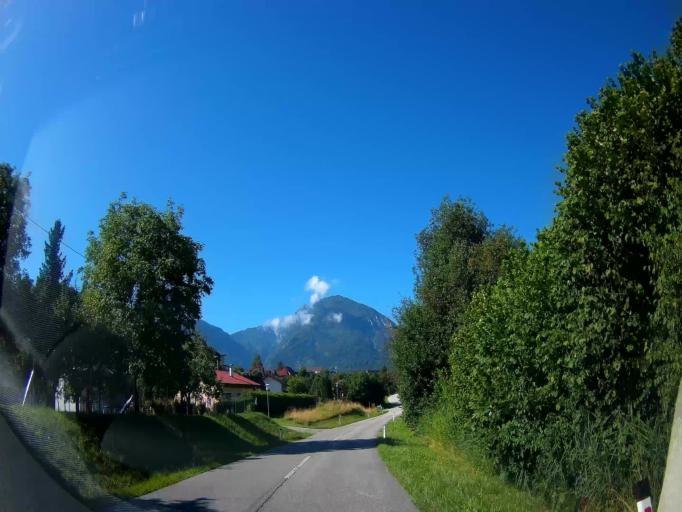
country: AT
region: Carinthia
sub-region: Politischer Bezirk Volkermarkt
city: Gallizien
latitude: 46.5783
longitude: 14.5107
